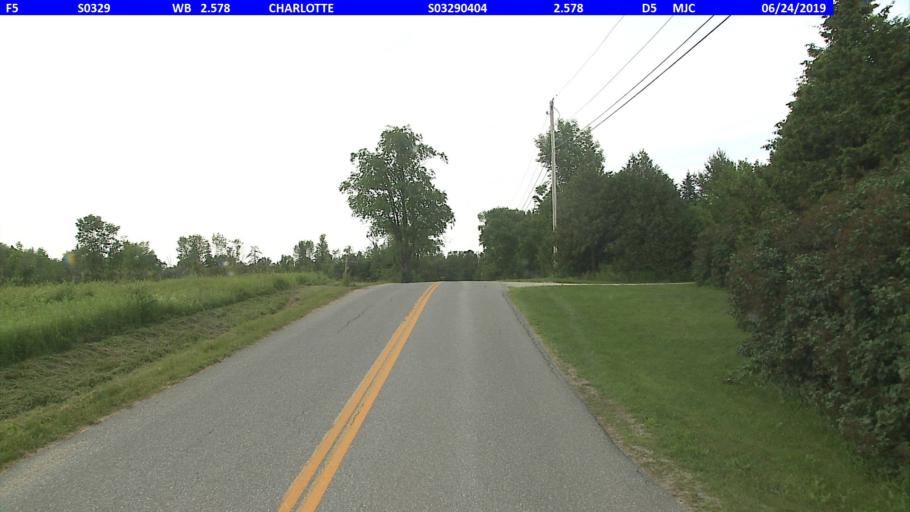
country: US
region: Vermont
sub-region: Addison County
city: Vergennes
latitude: 44.3041
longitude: -73.2939
